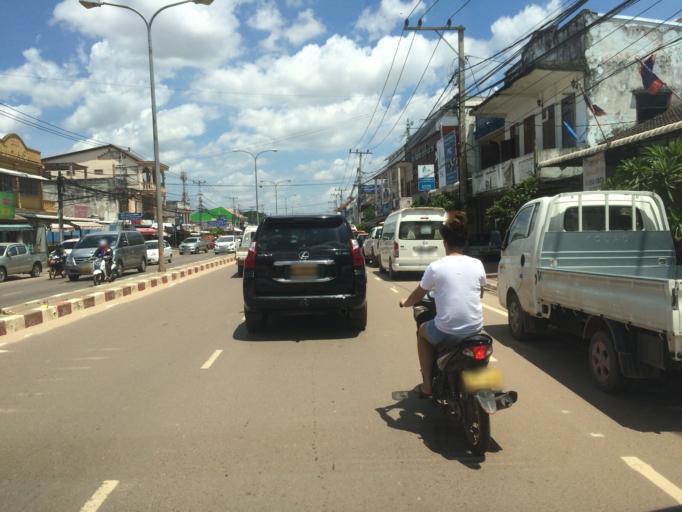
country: TH
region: Nong Khai
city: Si Chiang Mai
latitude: 17.9724
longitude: 102.5648
